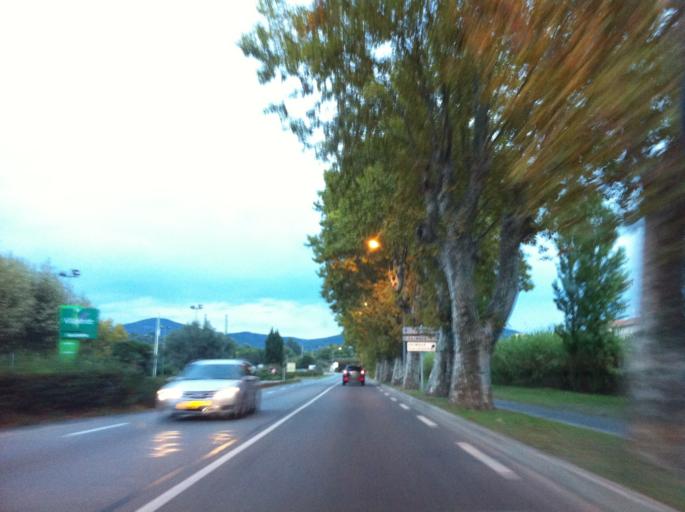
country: FR
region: Provence-Alpes-Cote d'Azur
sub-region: Departement du Var
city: Gassin
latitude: 43.2703
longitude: 6.5732
